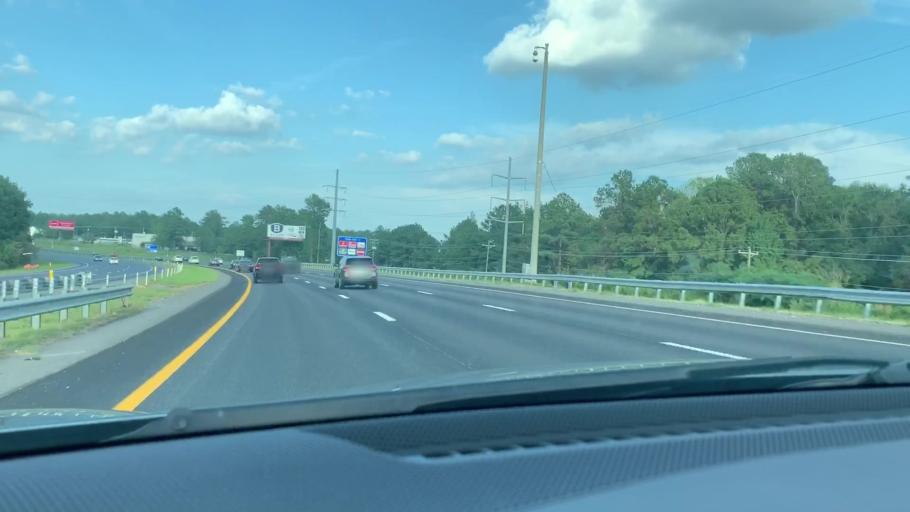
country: US
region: South Carolina
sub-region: Richland County
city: Forest Acres
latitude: 33.9554
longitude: -80.9572
